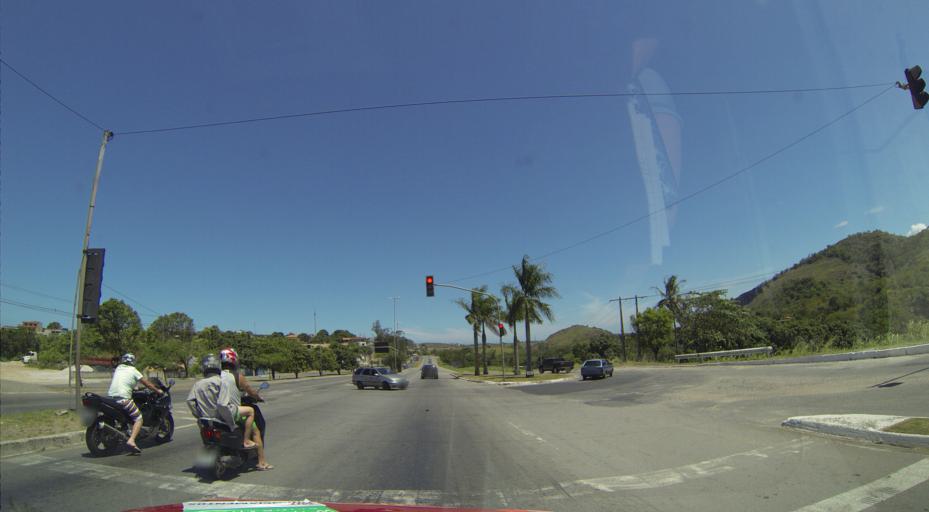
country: BR
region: Espirito Santo
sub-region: Serra
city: Serra
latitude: -20.1593
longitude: -40.2762
